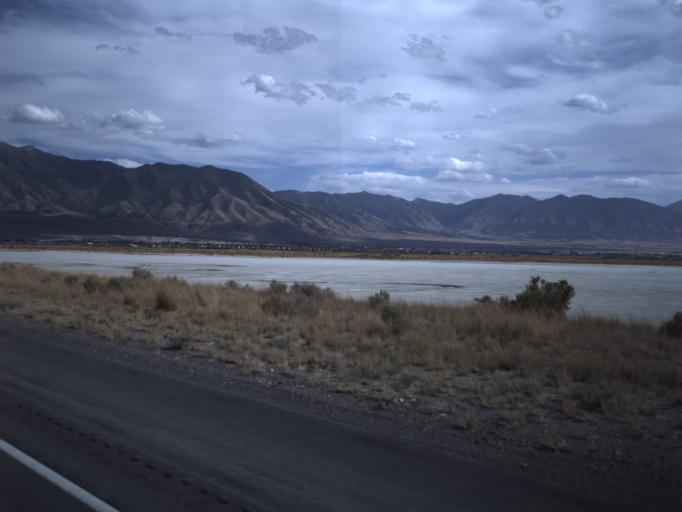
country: US
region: Utah
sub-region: Tooele County
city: Stansbury park
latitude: 40.6623
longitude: -112.3480
